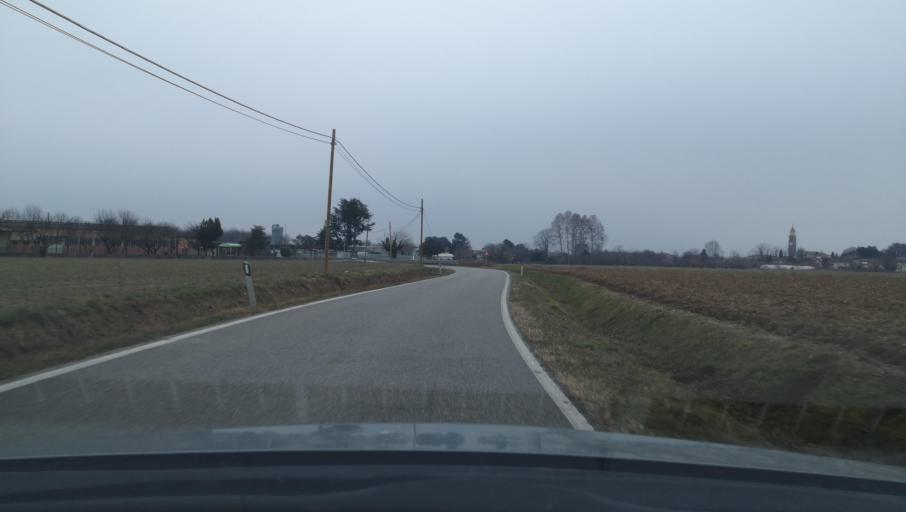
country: IT
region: Friuli Venezia Giulia
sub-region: Provincia di Udine
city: Trivignano Udinese
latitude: 45.9502
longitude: 13.3345
